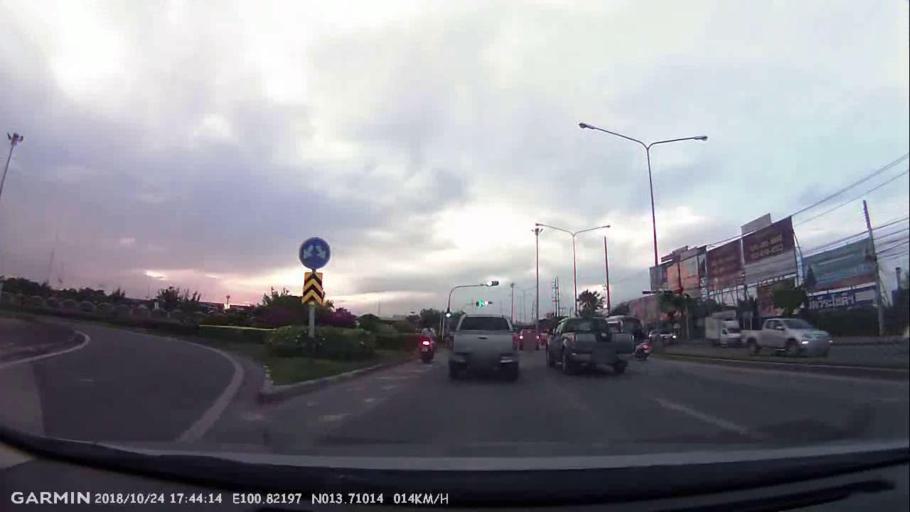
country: TH
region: Bangkok
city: Lat Krabang
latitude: 13.7101
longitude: 100.8220
